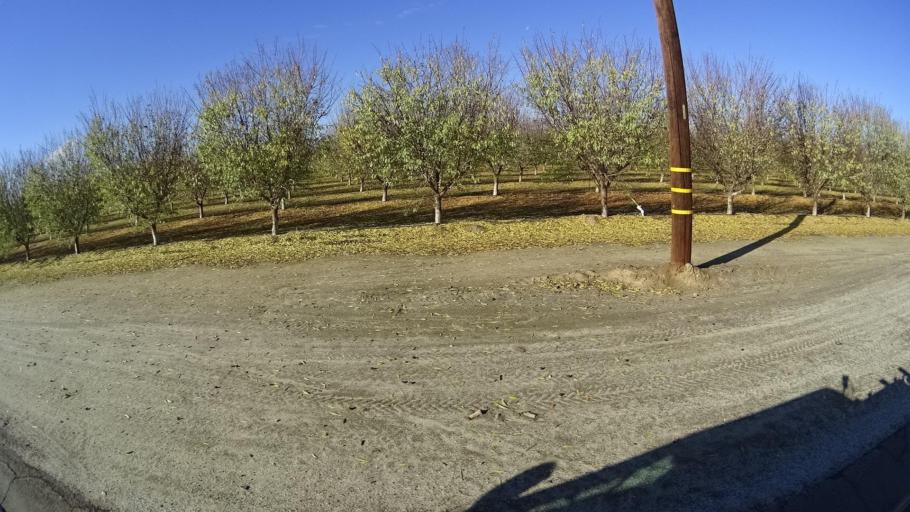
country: US
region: California
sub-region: Kern County
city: Delano
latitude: 35.7404
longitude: -119.2763
